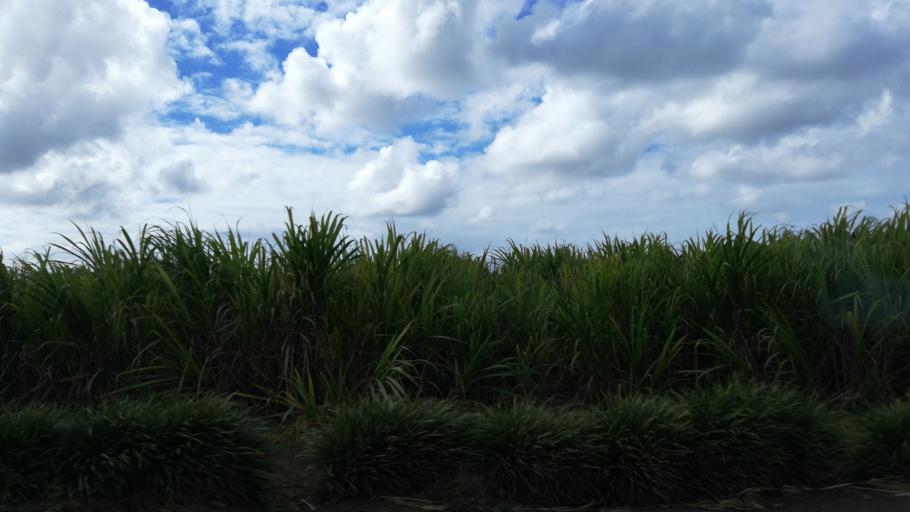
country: MU
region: Flacq
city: Camp de Masque
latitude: -20.2186
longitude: 57.6739
